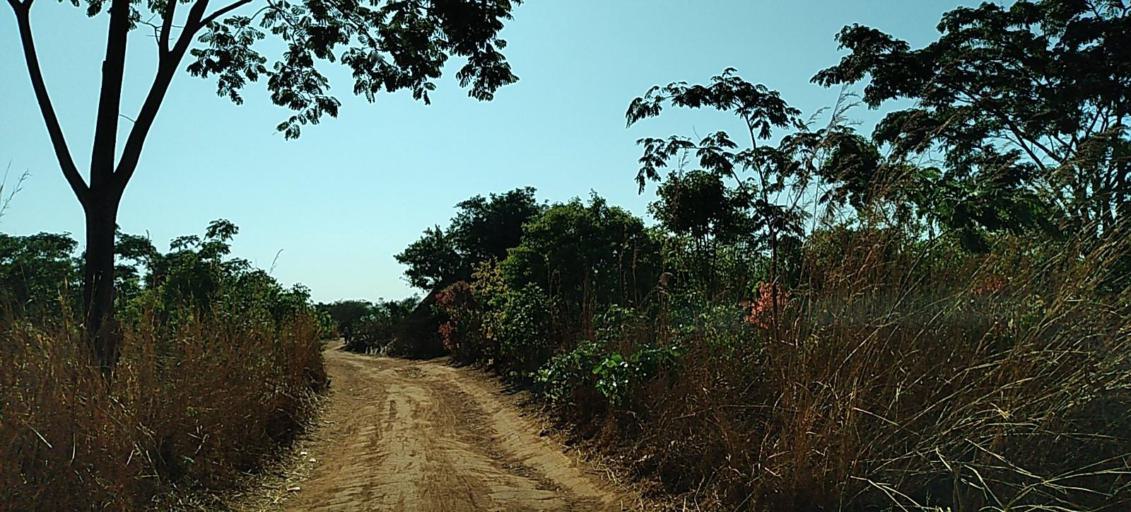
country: ZM
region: Copperbelt
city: Chililabombwe
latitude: -12.3706
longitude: 27.9033
